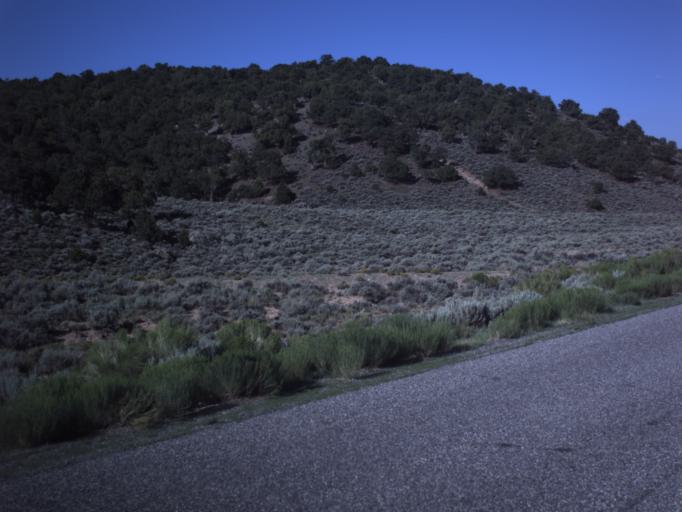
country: US
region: Utah
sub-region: Wayne County
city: Loa
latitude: 38.4791
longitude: -111.5596
